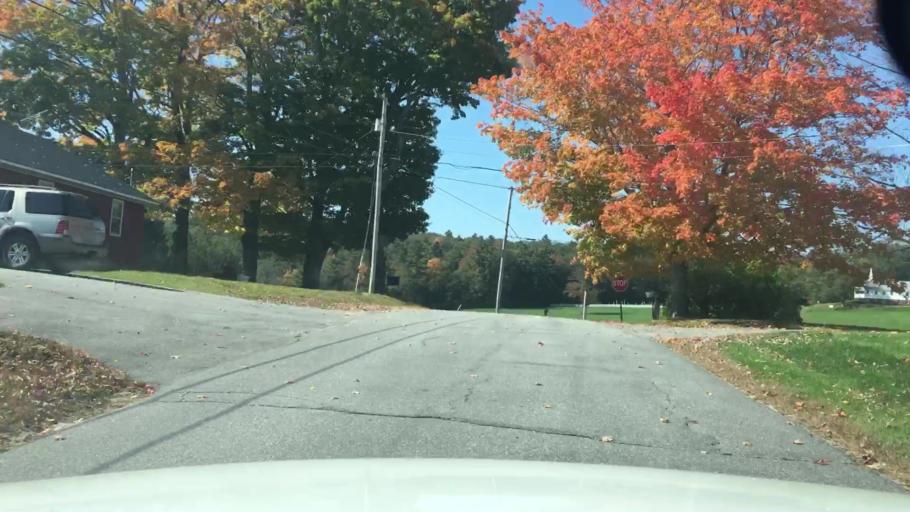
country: US
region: Maine
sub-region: Sagadahoc County
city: Topsham
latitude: 44.0134
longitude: -69.9694
